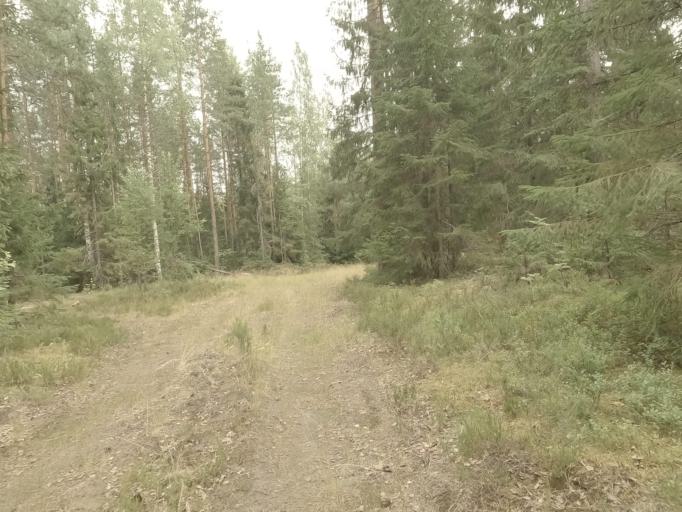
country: RU
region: Leningrad
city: Kamennogorsk
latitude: 61.0416
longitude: 29.1865
